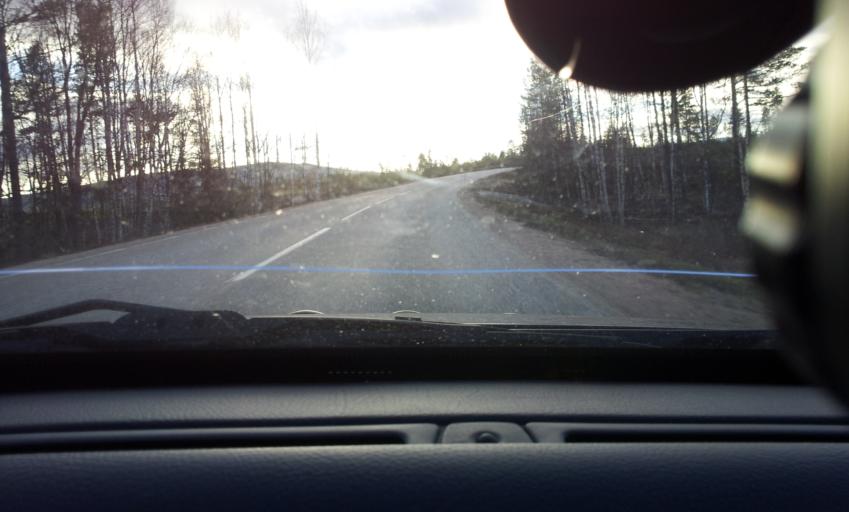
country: SE
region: Jaemtland
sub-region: Harjedalens Kommun
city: Sveg
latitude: 62.1248
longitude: 14.9892
